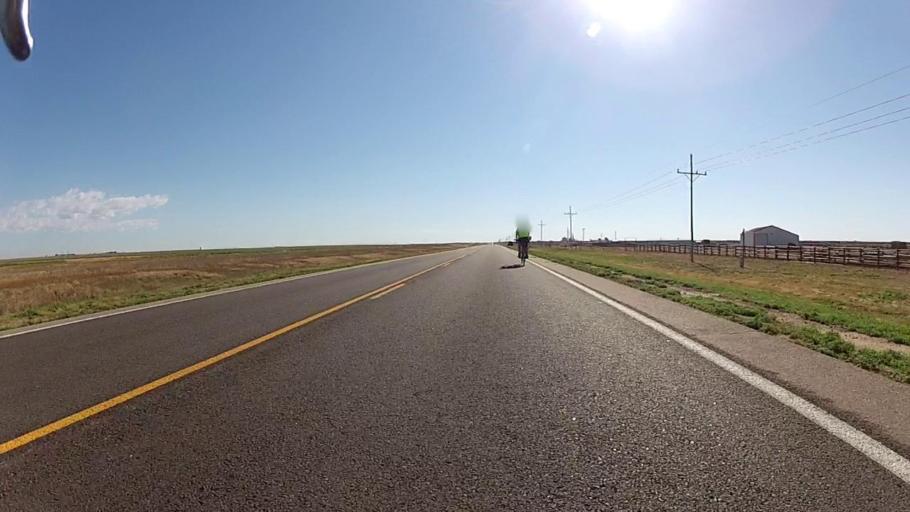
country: US
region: Kansas
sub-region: Haskell County
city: Sublette
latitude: 37.5679
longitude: -100.5473
